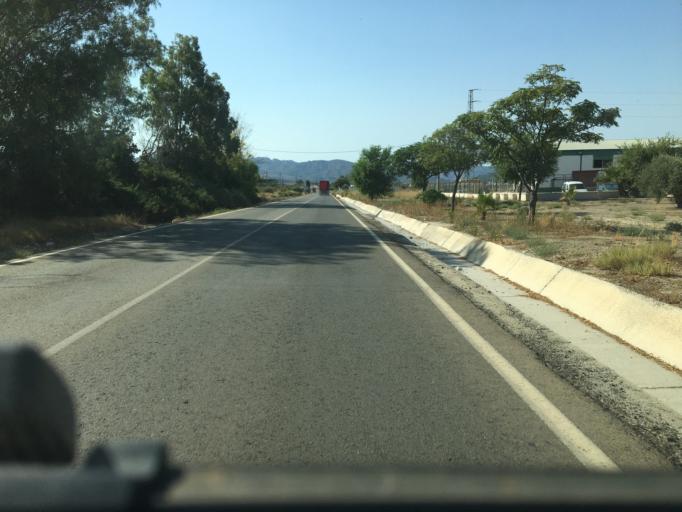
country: ES
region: Andalusia
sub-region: Provincia de Almeria
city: Huercal-Overa
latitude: 37.4136
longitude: -1.9640
